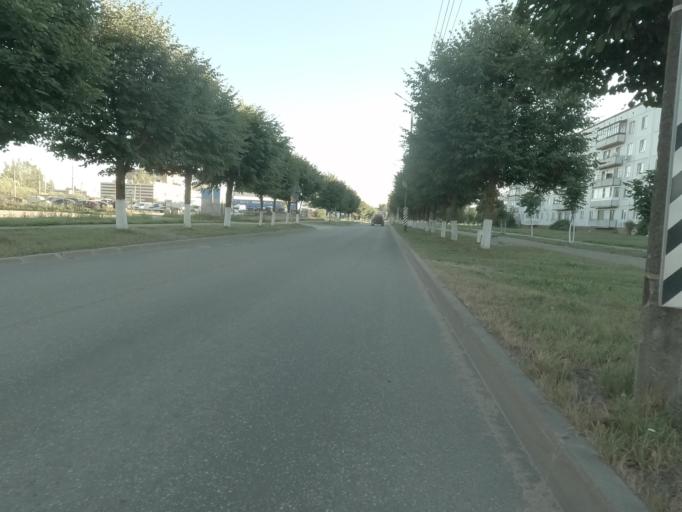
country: RU
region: Leningrad
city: Kirovsk
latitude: 59.8834
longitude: 30.9994
